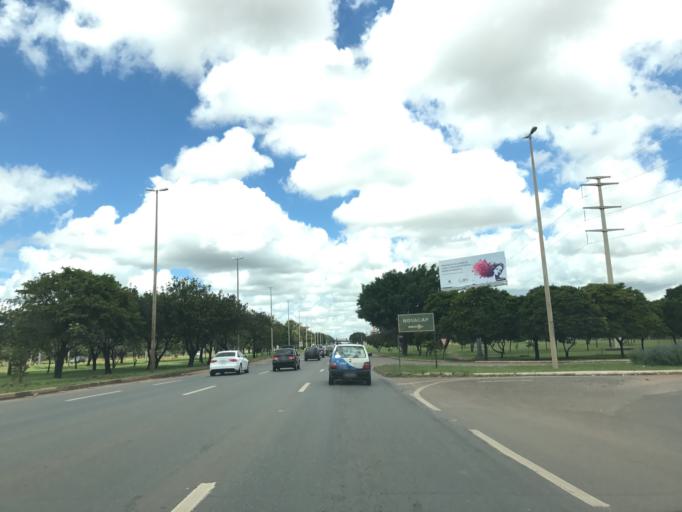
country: BR
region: Federal District
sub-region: Brasilia
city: Brasilia
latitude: -15.8166
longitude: -47.9497
